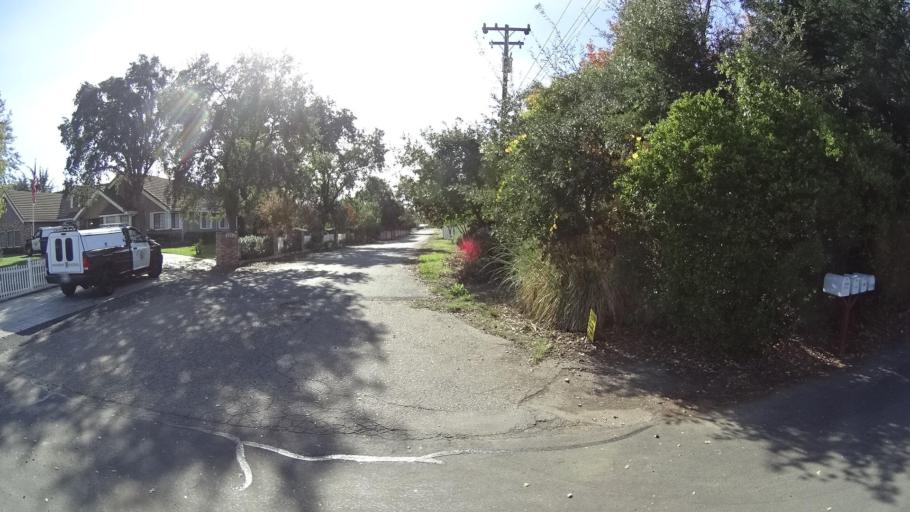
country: US
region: California
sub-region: Sacramento County
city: Wilton
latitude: 38.4268
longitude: -121.2842
